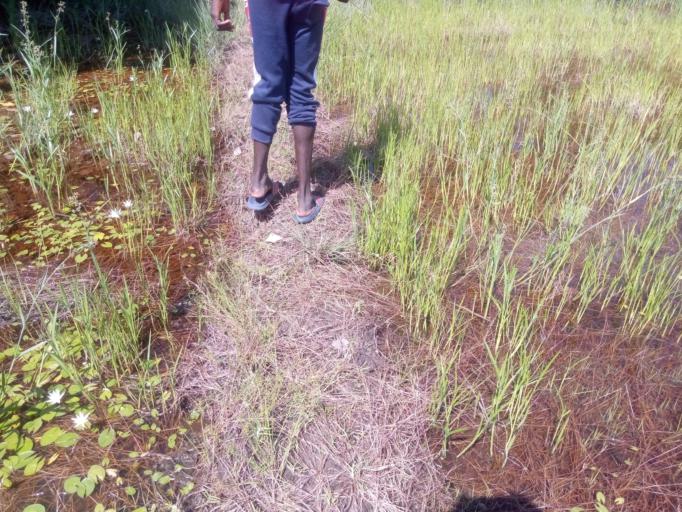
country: GM
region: Western
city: Gunjur
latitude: 13.0372
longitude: -16.7324
